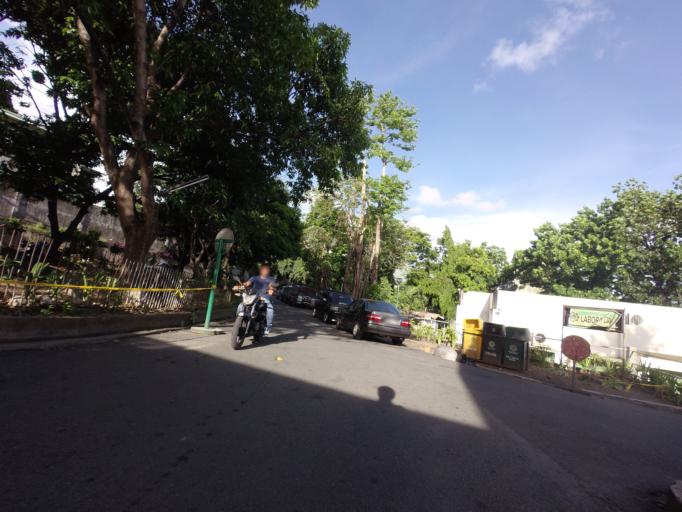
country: PH
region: Metro Manila
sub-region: Mandaluyong
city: Mandaluyong City
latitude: 14.5792
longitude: 121.0422
